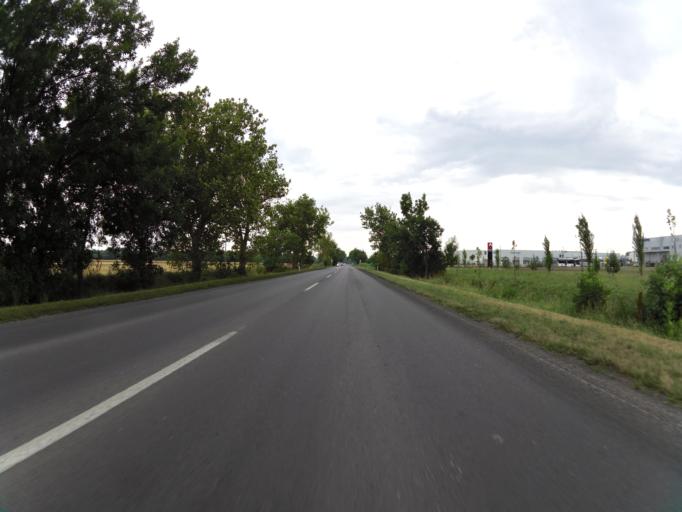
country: HU
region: Csongrad
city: Szeged
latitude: 46.2870
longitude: 20.0883
